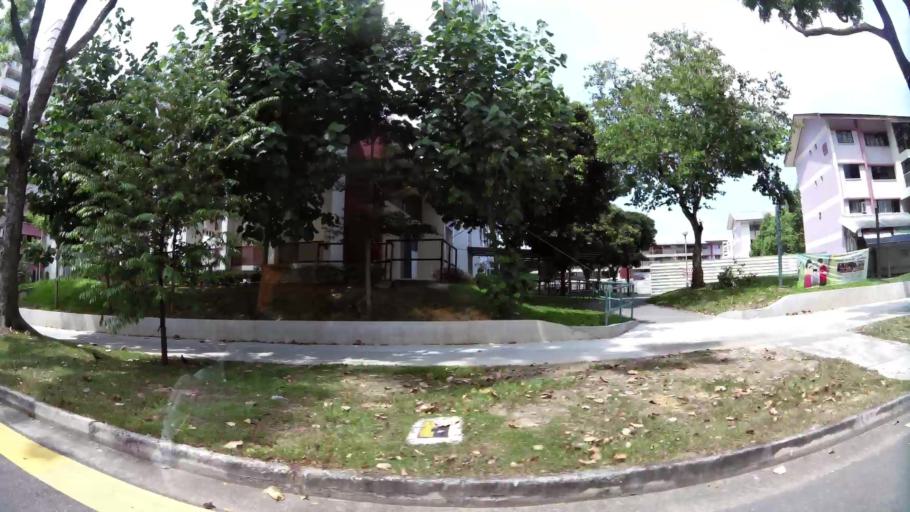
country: MY
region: Johor
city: Johor Bahru
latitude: 1.3488
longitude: 103.7255
